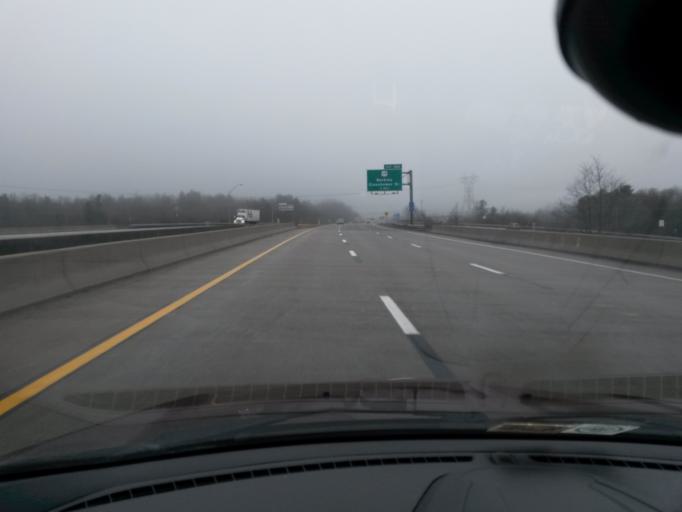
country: US
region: West Virginia
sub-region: Raleigh County
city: Daniels
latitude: 37.7670
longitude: -81.1240
